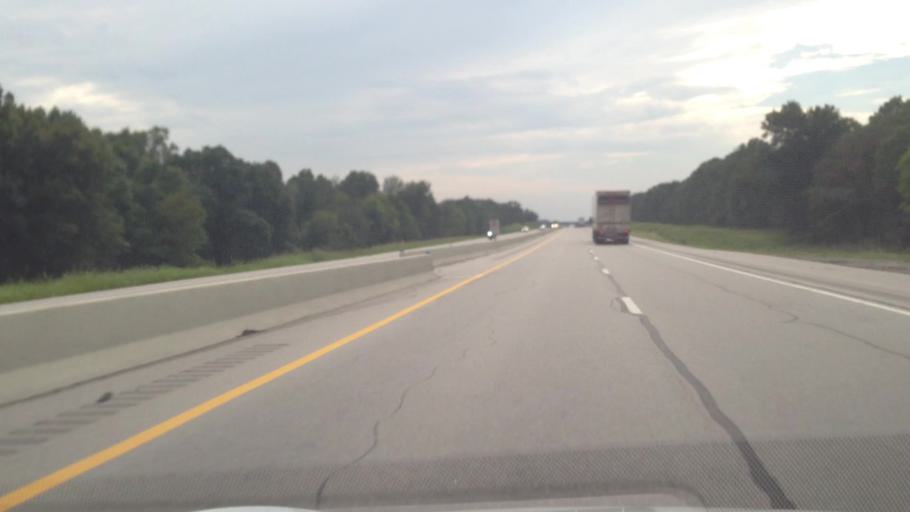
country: US
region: Kansas
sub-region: Cherokee County
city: Baxter Springs
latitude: 36.9321
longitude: -94.7200
